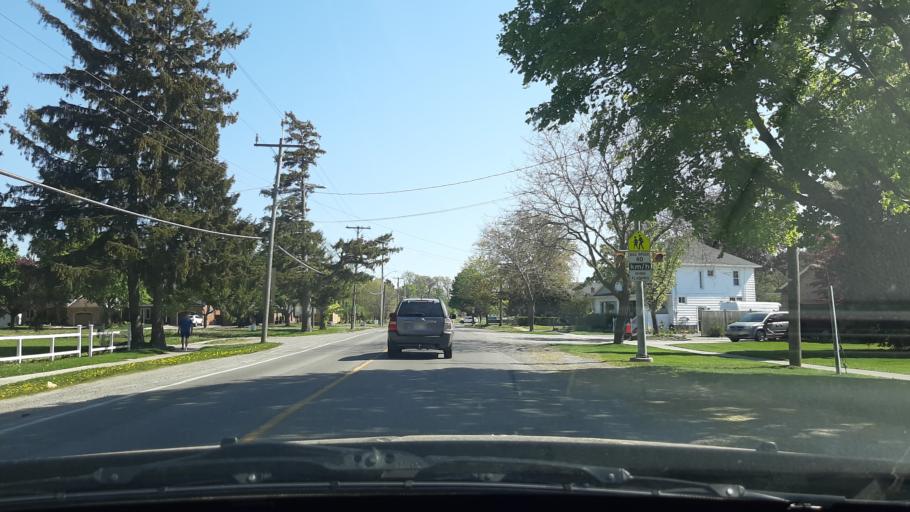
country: CA
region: Ontario
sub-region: Regional Municipality of Niagara
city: St. Catharines
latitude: 43.1869
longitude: -79.2258
